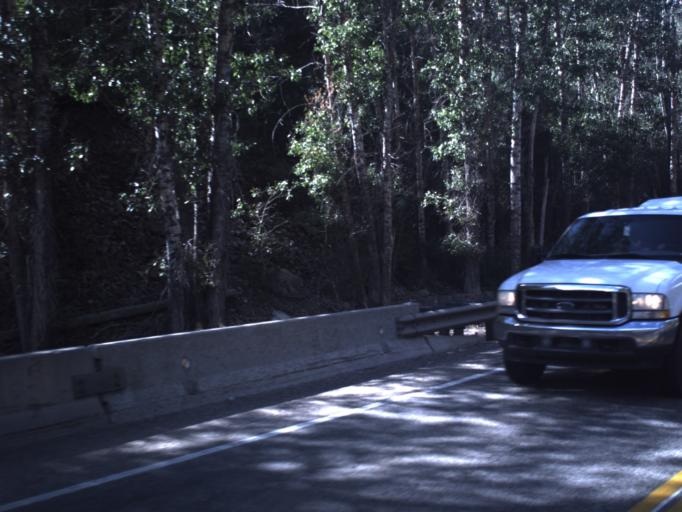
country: US
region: Utah
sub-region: Wasatch County
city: Heber
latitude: 40.3727
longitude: -111.2945
